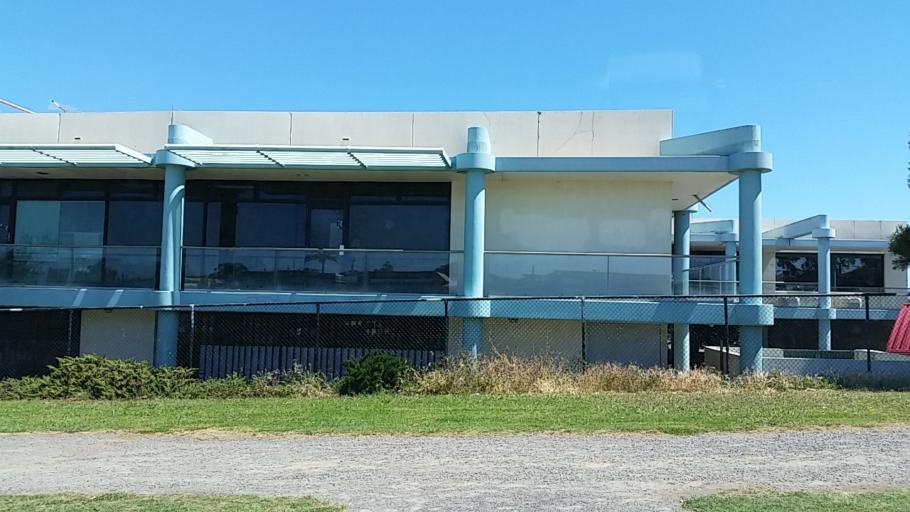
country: AU
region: South Australia
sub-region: Adelaide
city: Port Noarlunga
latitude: -35.1382
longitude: 138.4826
